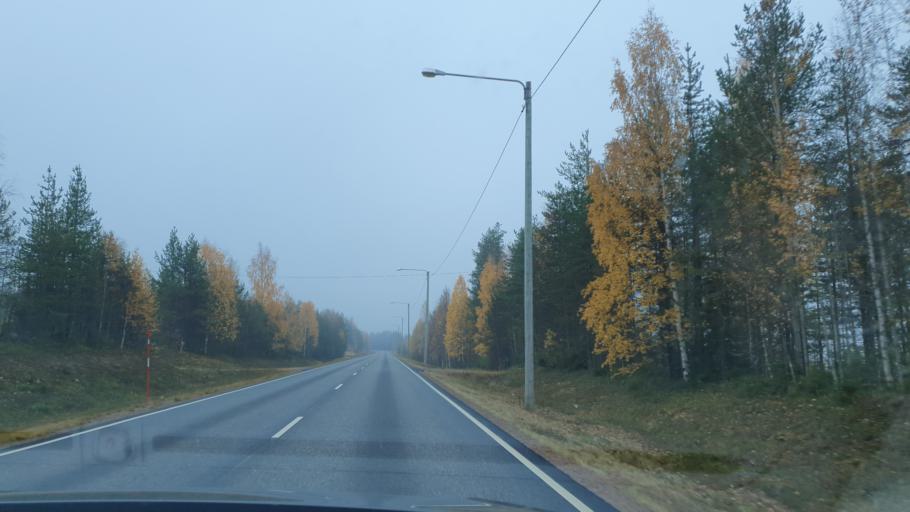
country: FI
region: Lapland
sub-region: Tunturi-Lappi
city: Kittilae
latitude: 67.0358
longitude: 25.1042
